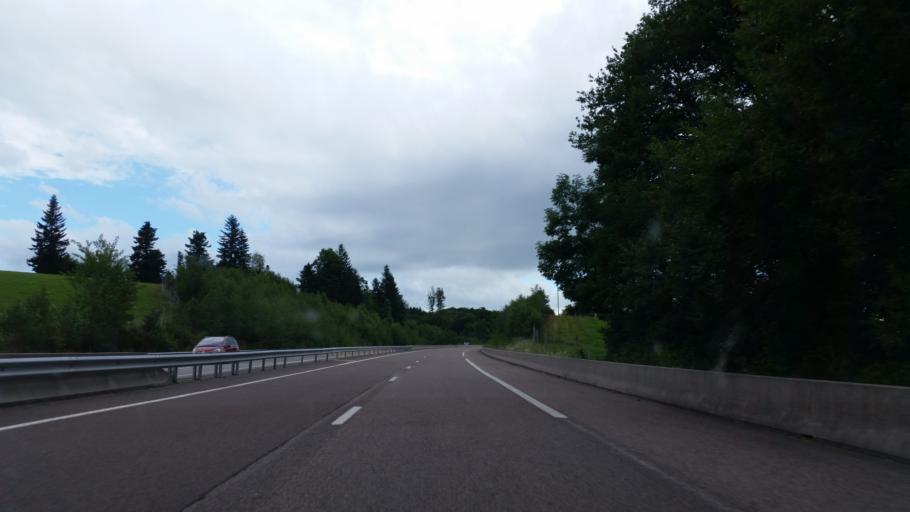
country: FR
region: Lorraine
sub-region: Departement des Vosges
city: Plombieres-les-Bains
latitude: 47.9702
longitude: 6.4930
